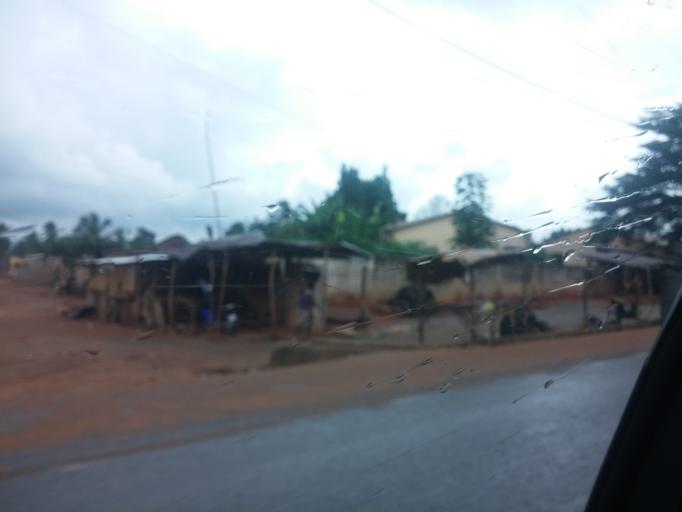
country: TG
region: Maritime
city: Tsevie
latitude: 6.4314
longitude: 1.2128
